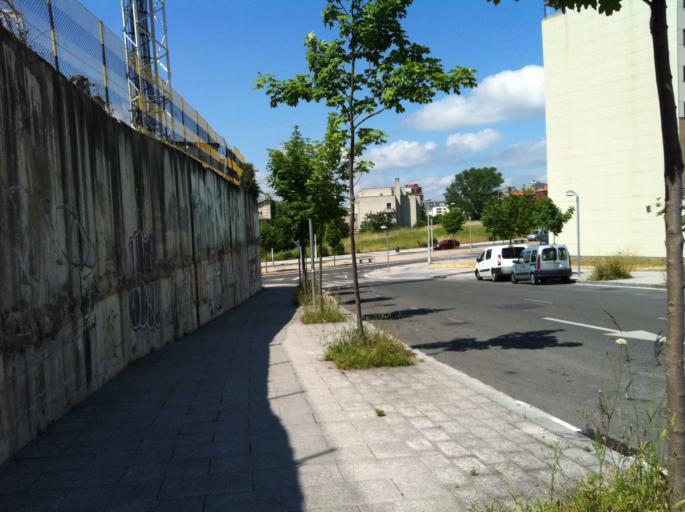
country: ES
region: Basque Country
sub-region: Provincia de Alava
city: Gasteiz / Vitoria
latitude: 42.8477
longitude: -2.6560
